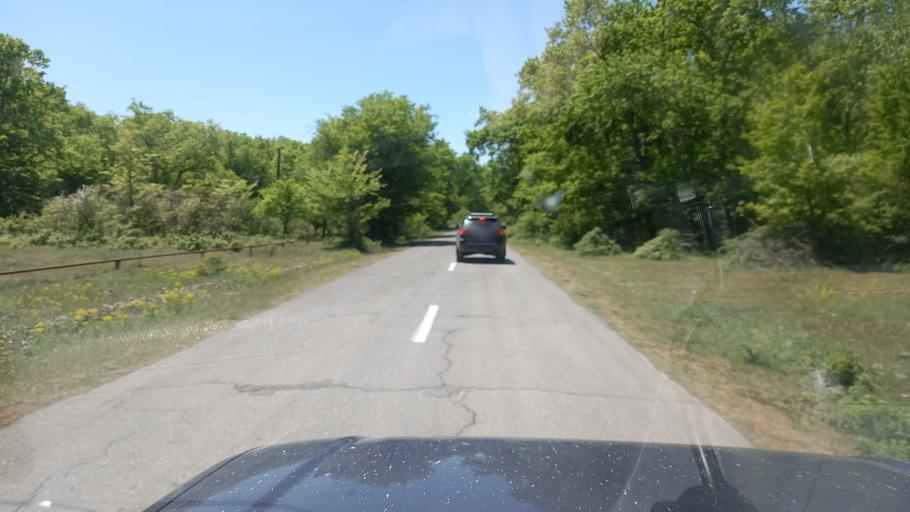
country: RU
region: Dagestan
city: Samur
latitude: 41.8423
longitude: 48.5741
